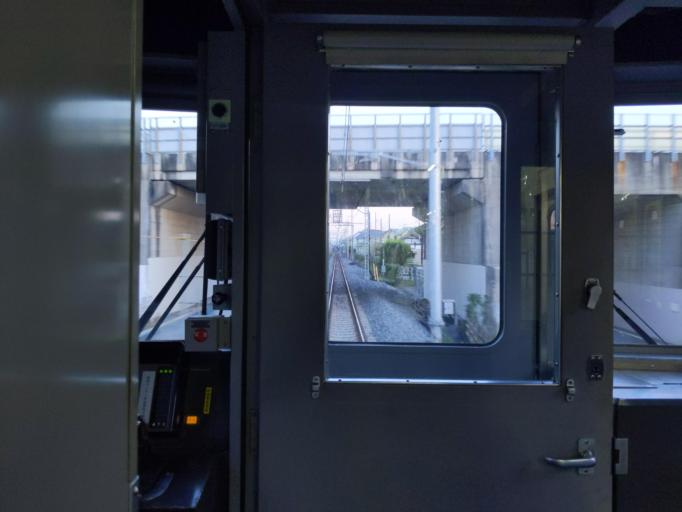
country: JP
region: Chiba
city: Noda
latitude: 35.9391
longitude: 139.8801
